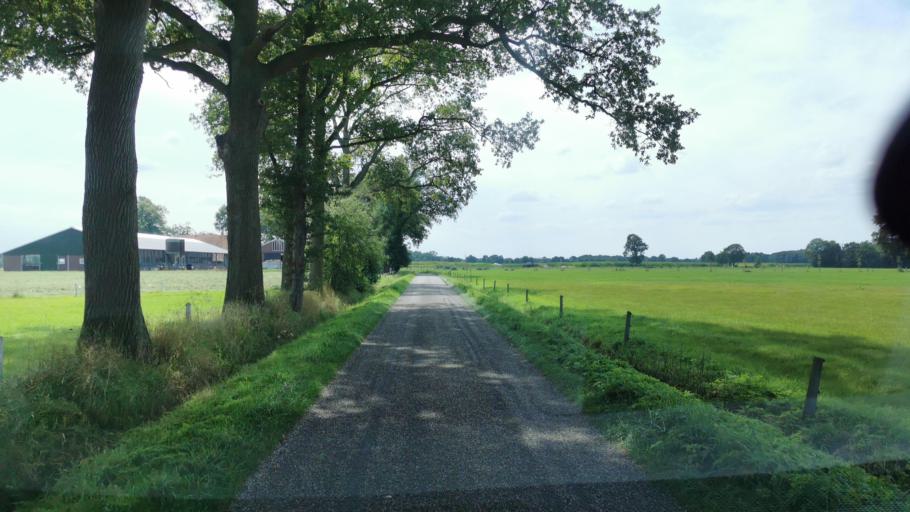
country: NL
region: Overijssel
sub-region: Gemeente Enschede
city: Enschede
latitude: 52.1691
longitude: 6.8931
